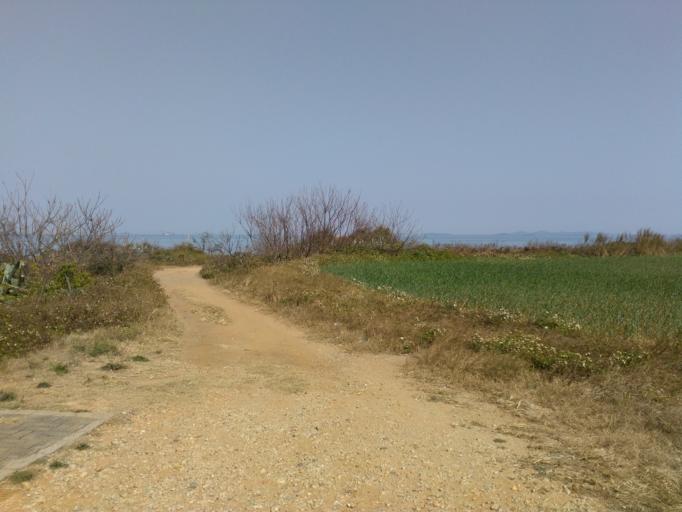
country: TW
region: Fukien
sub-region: Kinmen
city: Jincheng
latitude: 24.4888
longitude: 118.3131
